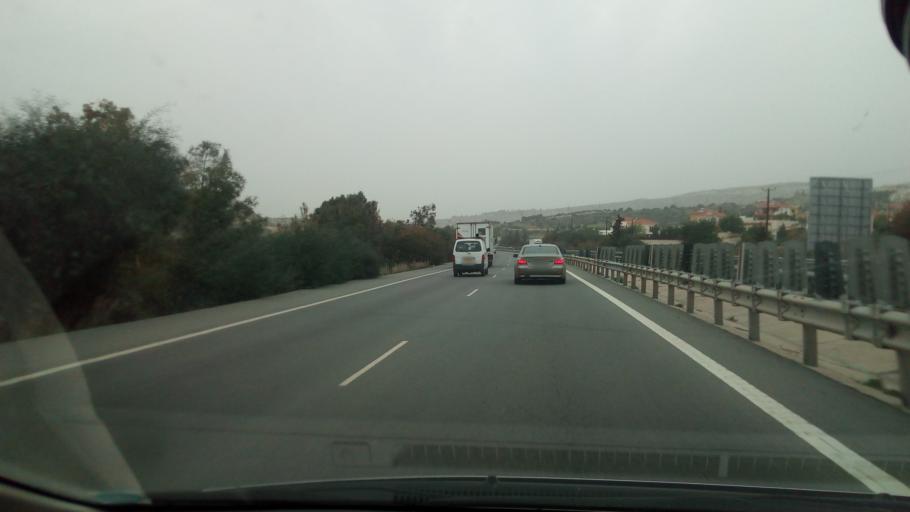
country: CY
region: Larnaka
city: Agios Tychon
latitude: 34.7182
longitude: 33.1488
